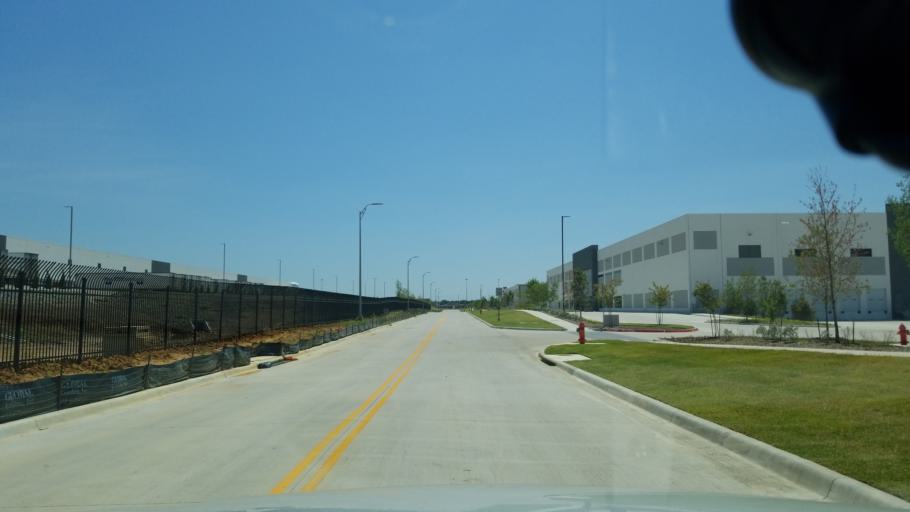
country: US
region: Texas
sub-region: Tarrant County
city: Euless
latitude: 32.8420
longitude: -97.0278
